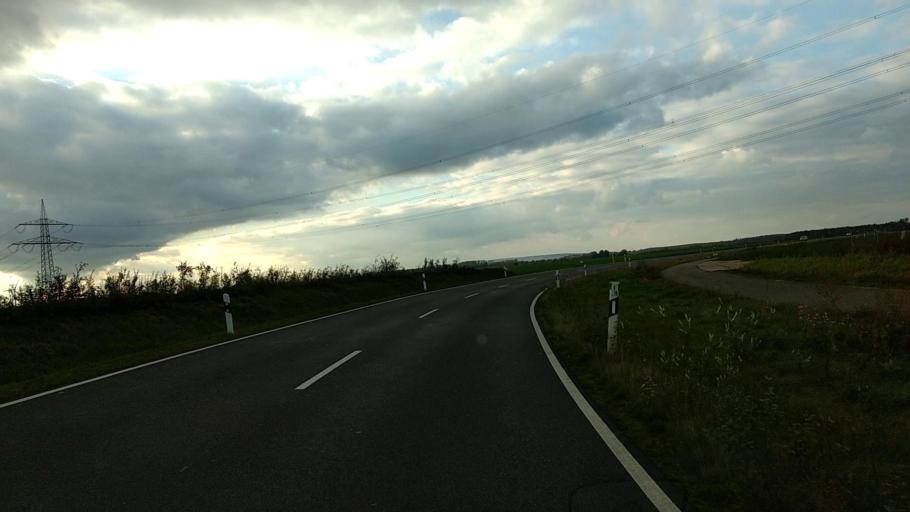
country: DE
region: North Rhine-Westphalia
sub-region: Regierungsbezirk Koln
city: Kerpen
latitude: 50.8657
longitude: 6.6490
